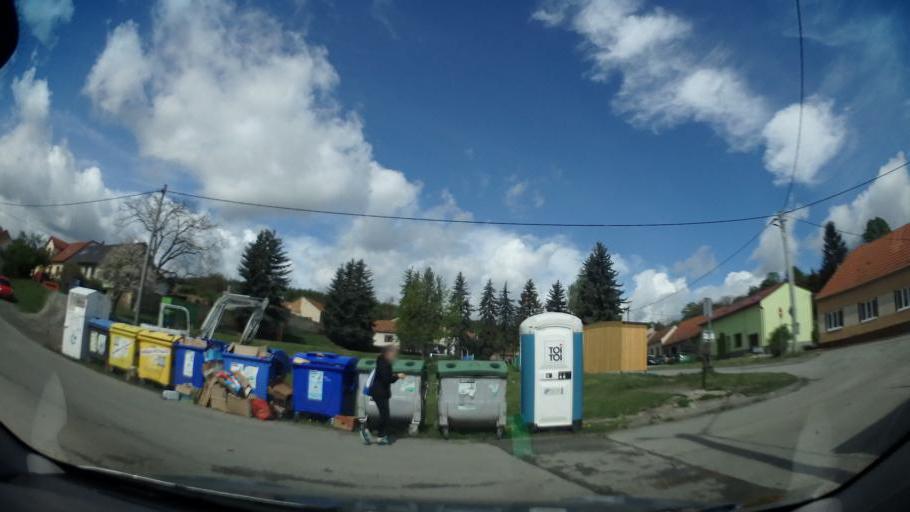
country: CZ
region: South Moravian
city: Ricany
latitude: 49.2391
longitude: 16.3911
